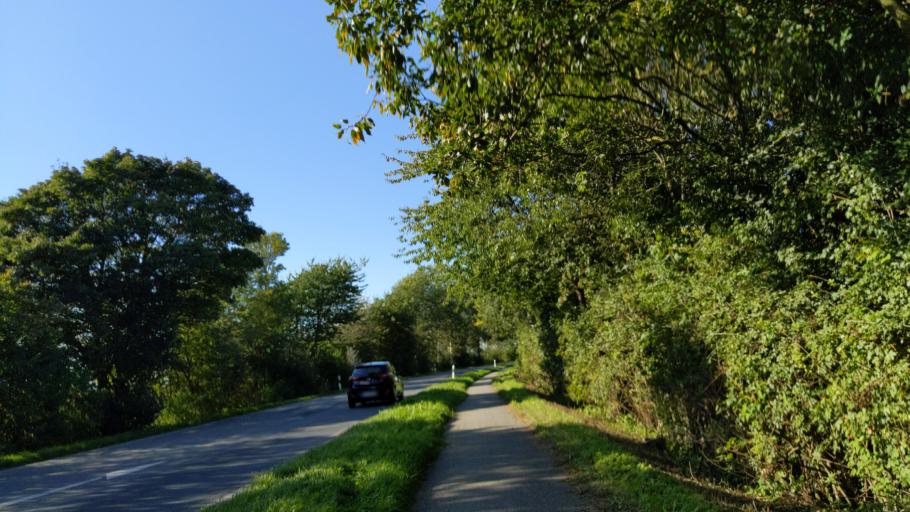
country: DE
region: Schleswig-Holstein
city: Ahrensbok
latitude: 53.9706
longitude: 10.5958
